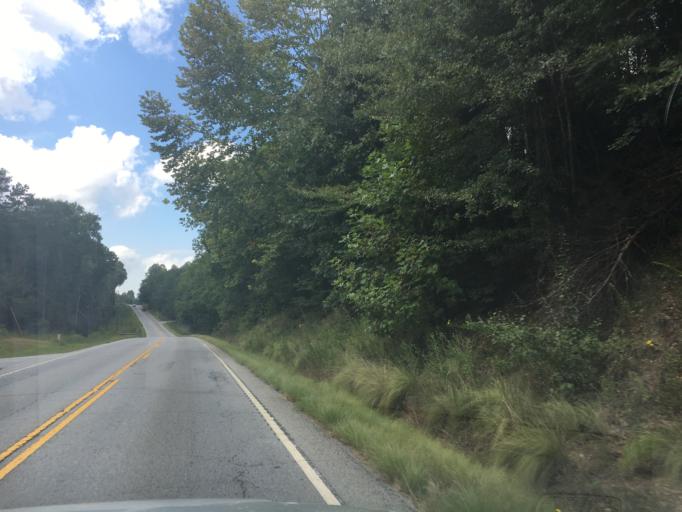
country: US
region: South Carolina
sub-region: Greenville County
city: Berea
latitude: 34.8870
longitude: -82.5079
